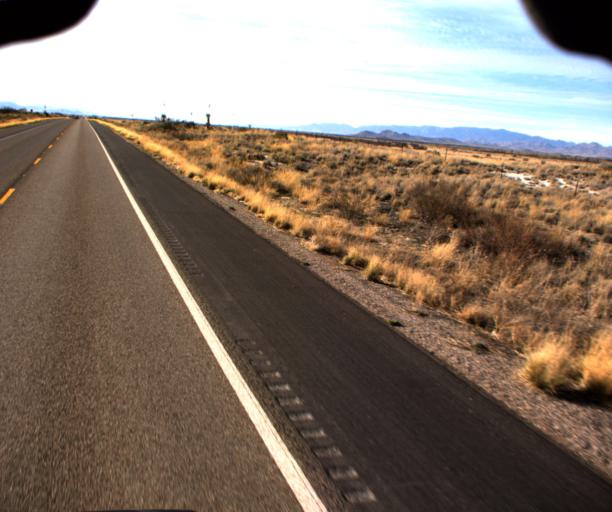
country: US
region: Arizona
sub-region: Cochise County
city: Willcox
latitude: 32.2170
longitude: -109.7854
